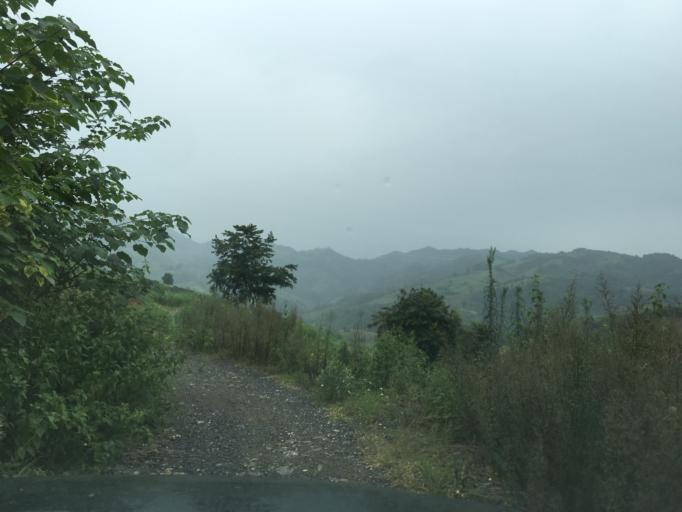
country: CN
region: Guangxi Zhuangzu Zizhiqu
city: Tongle
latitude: 25.0037
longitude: 105.9916
